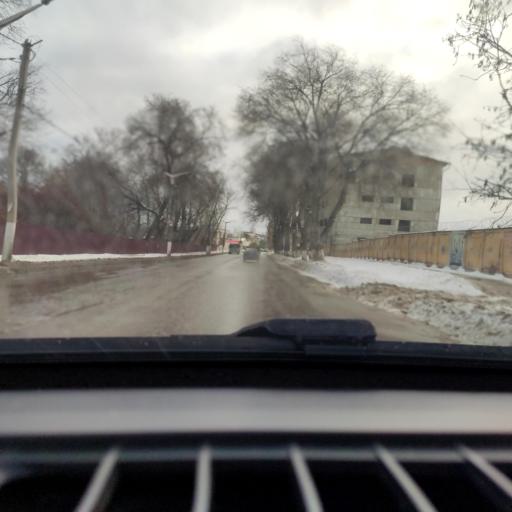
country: RU
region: Voronezj
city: Semiluki
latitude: 51.6907
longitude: 39.0365
